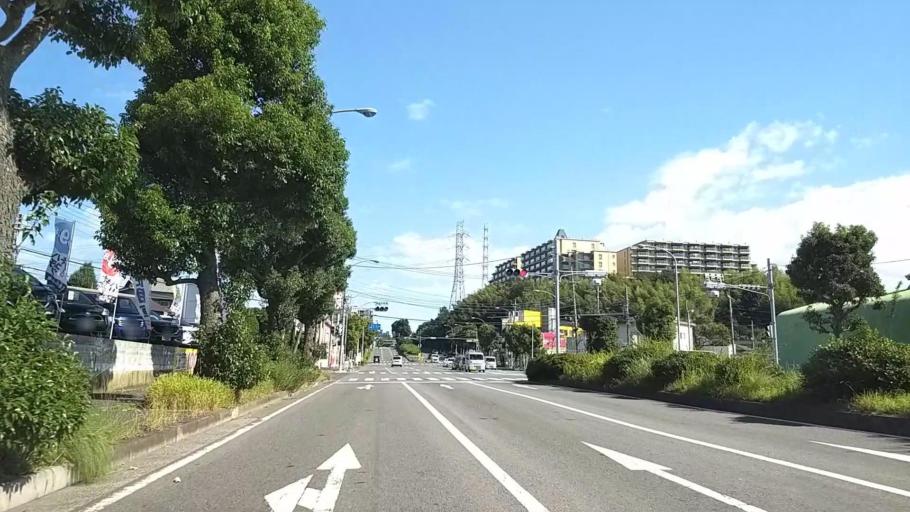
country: JP
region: Kanagawa
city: Yokohama
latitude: 35.5292
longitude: 139.5925
